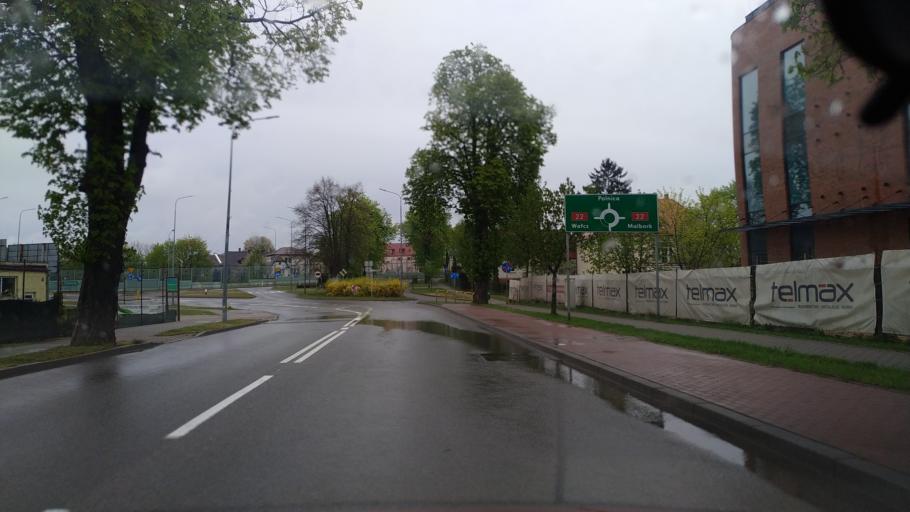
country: PL
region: Pomeranian Voivodeship
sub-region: Powiat czluchowski
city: Czluchow
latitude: 53.6722
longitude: 17.3678
